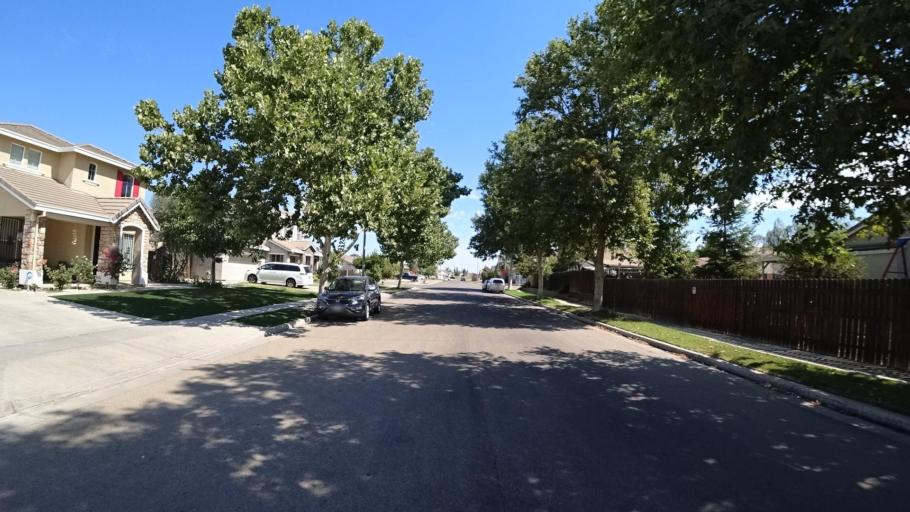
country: US
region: California
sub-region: Fresno County
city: Sunnyside
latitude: 36.7108
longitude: -119.7134
